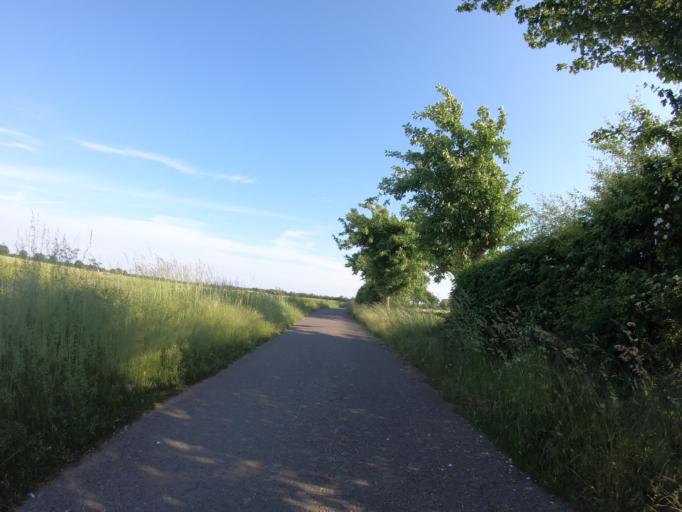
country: DE
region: Lower Saxony
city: Meine
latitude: 52.3675
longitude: 10.5455
